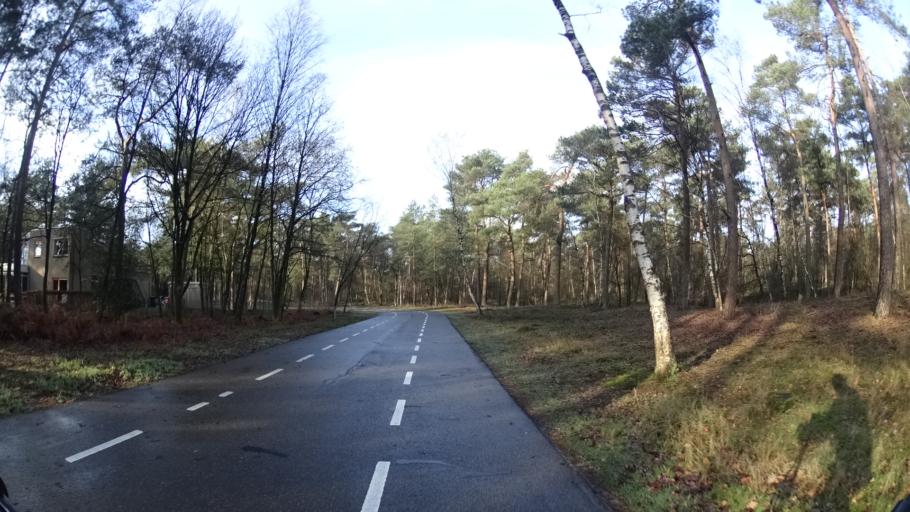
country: NL
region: Gelderland
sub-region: Gemeente Ede
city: Wekerom
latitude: 52.0919
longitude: 5.7357
